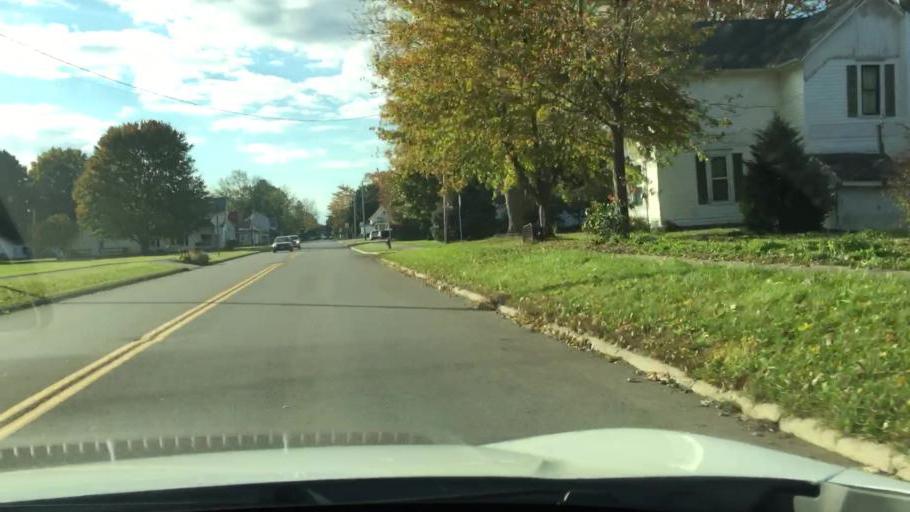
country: US
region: Ohio
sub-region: Champaign County
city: North Lewisburg
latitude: 40.2228
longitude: -83.5490
